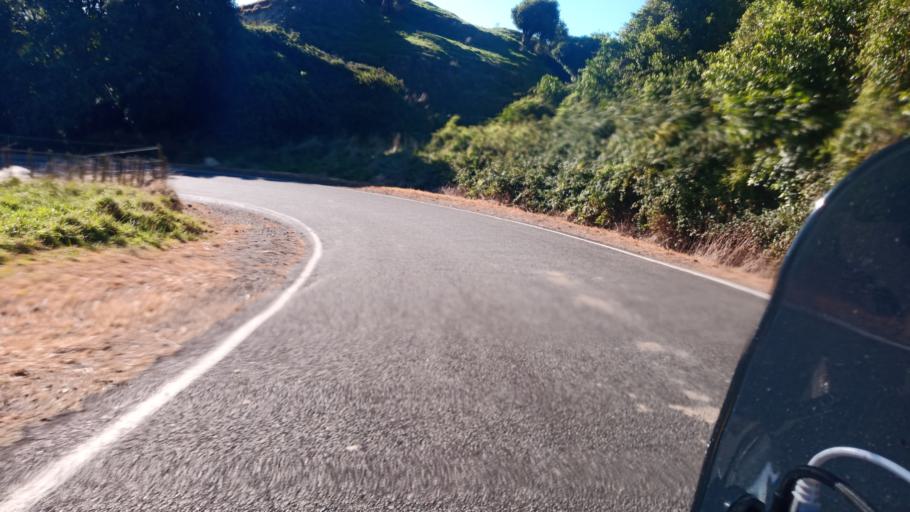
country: NZ
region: Hawke's Bay
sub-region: Wairoa District
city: Wairoa
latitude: -38.8267
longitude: 177.2931
